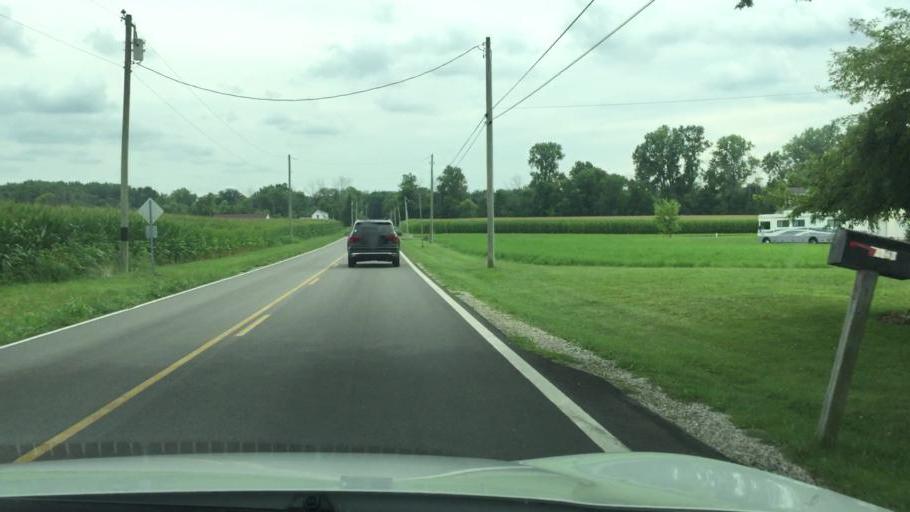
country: US
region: Ohio
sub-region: Union County
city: Marysville
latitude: 40.1881
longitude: -83.4354
